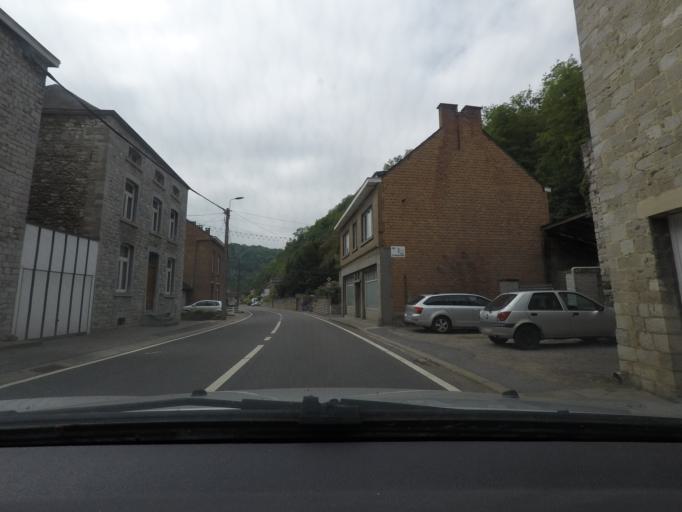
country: BE
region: Wallonia
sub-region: Province de Namur
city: Noville-les-Bois
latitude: 50.4654
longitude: 4.9999
